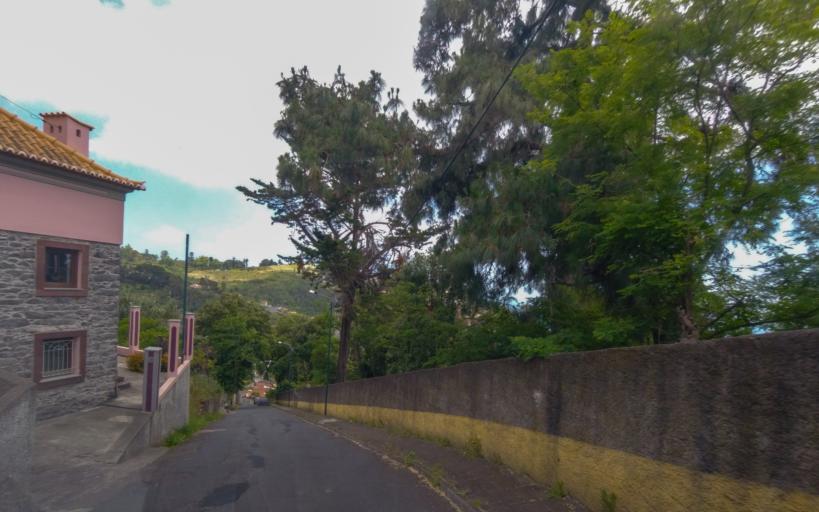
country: PT
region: Madeira
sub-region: Funchal
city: Nossa Senhora do Monte
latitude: 32.6628
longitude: -16.8796
